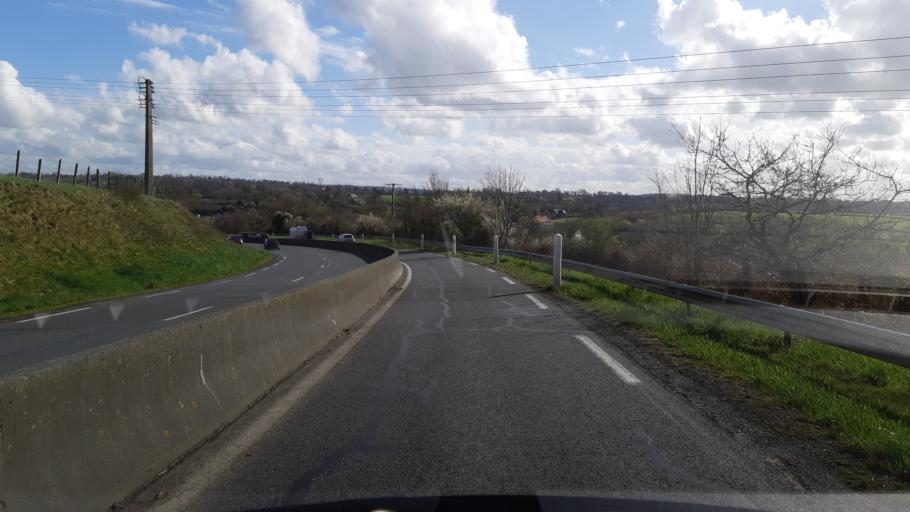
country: FR
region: Lower Normandy
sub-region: Departement de la Manche
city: Agneaux
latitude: 49.0967
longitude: -1.1215
